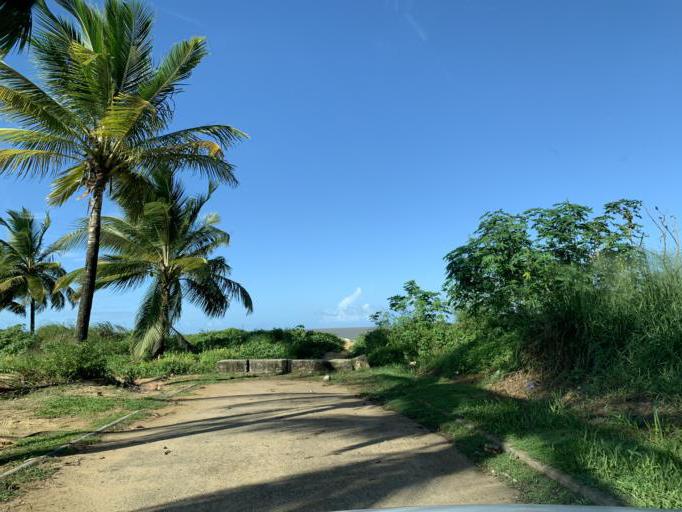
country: GF
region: Guyane
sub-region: Guyane
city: Kourou
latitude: 5.1743
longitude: -52.6456
